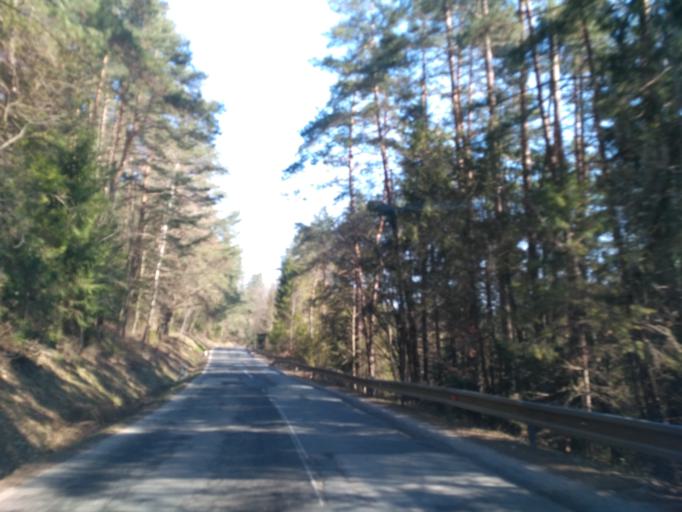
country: SK
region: Kosicky
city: Medzev
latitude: 48.7879
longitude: 20.8019
